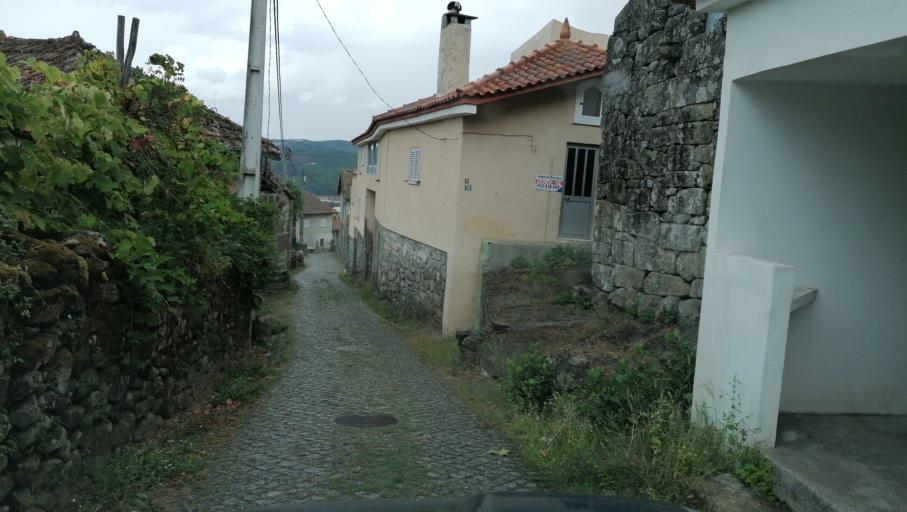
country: PT
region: Vila Real
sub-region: Ribeira de Pena
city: Sobreira
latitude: 41.5613
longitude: -7.7174
